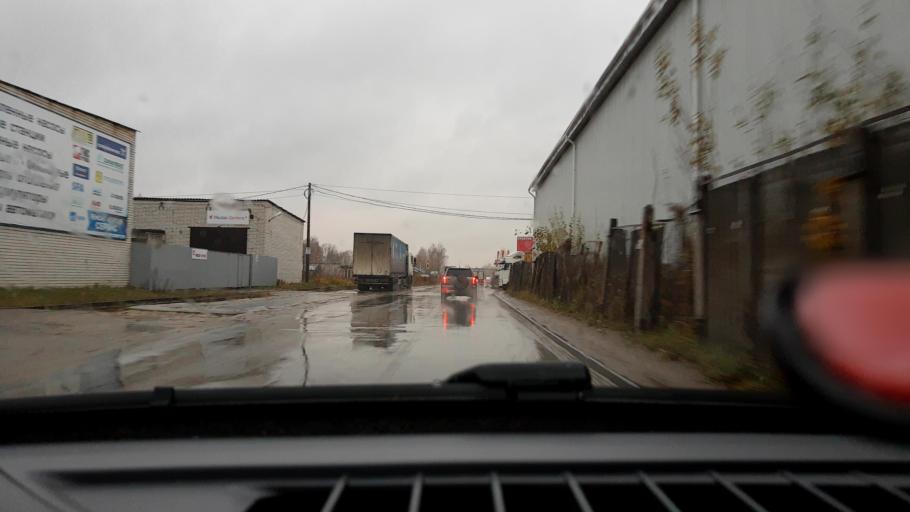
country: RU
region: Nizjnij Novgorod
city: Gorbatovka
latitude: 56.3159
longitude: 43.8568
